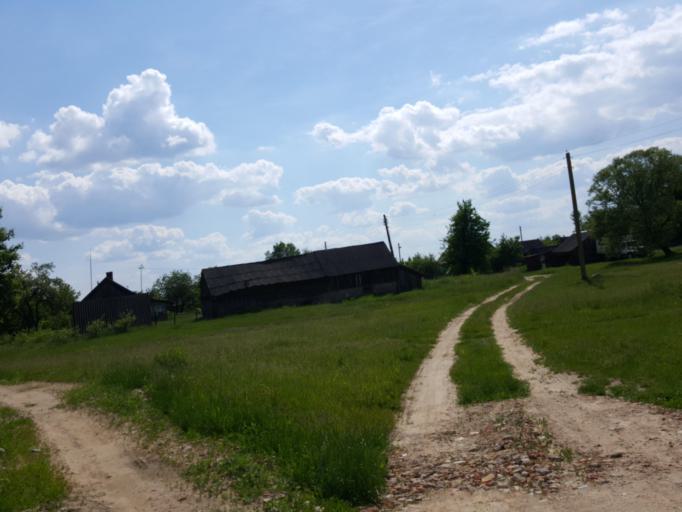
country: BY
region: Brest
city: Kamyanyuki
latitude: 52.5054
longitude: 23.6580
